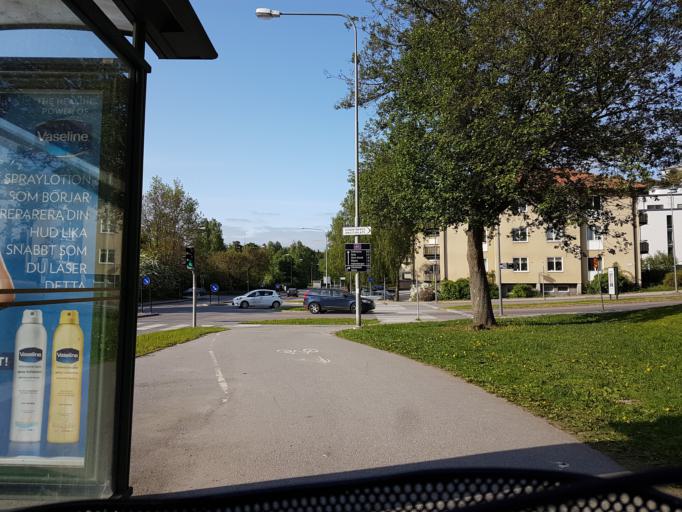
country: SE
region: Stockholm
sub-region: Sundbybergs Kommun
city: Sundbyberg
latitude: 59.3688
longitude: 17.9607
